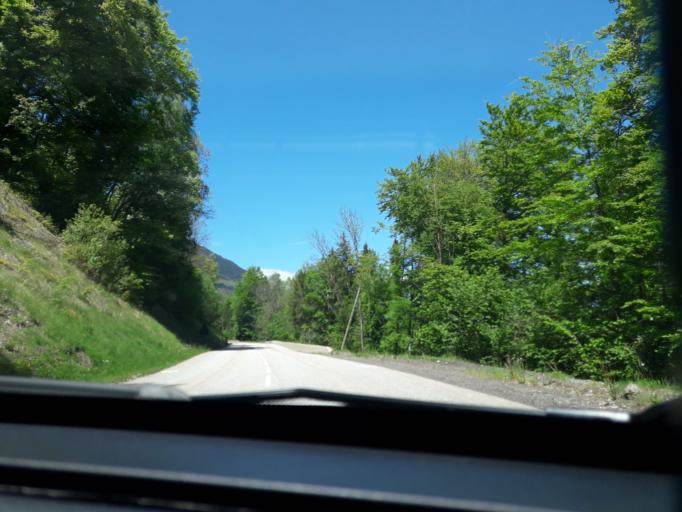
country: FR
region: Rhone-Alpes
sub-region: Departement de la Savoie
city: Saint-Martin-de-Belleville
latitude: 45.4203
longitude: 6.4860
